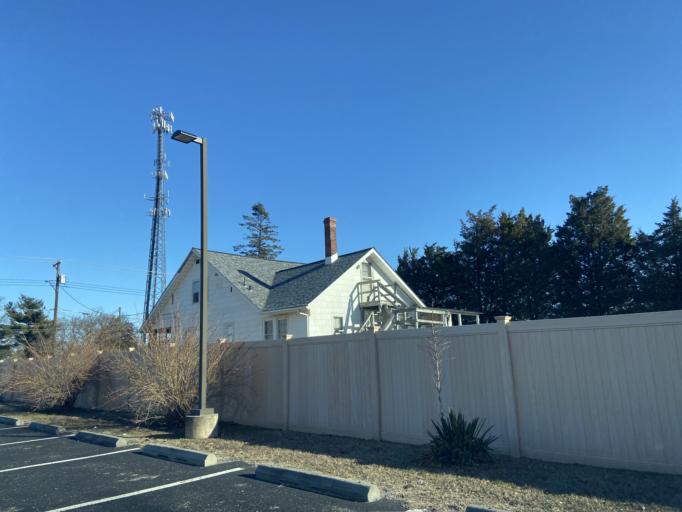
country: US
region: New Jersey
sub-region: Cumberland County
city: Vineland
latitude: 39.4875
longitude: -75.0640
